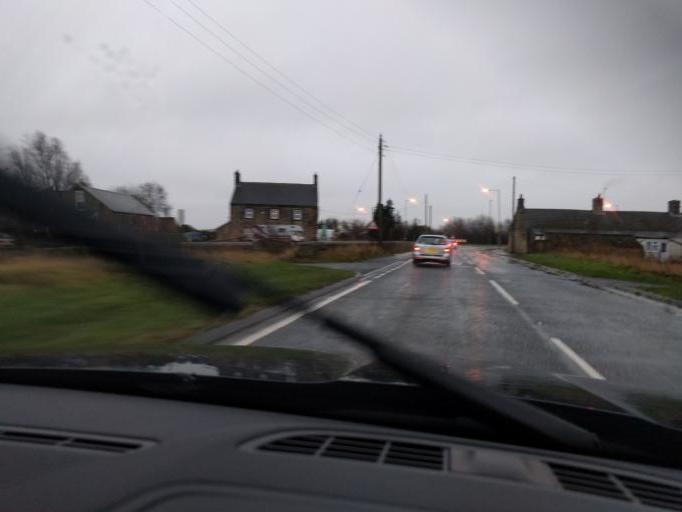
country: GB
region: England
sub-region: Northumberland
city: Cramlington
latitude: 55.1015
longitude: -1.5602
